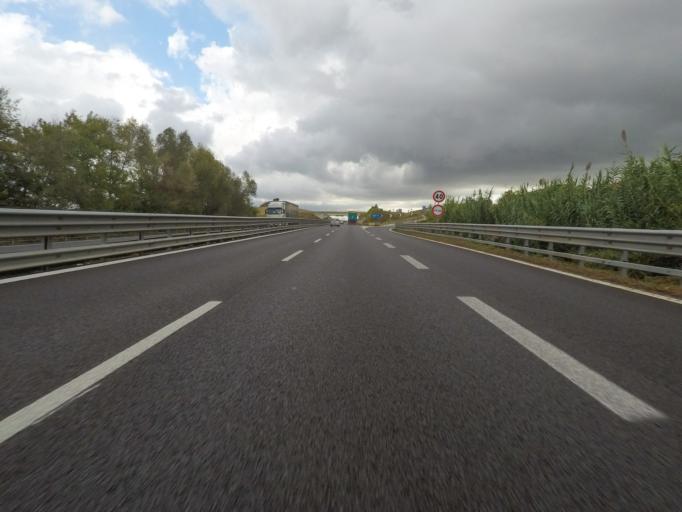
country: IT
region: Tuscany
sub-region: Provincia di Siena
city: Arbia
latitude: 43.3052
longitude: 11.4247
